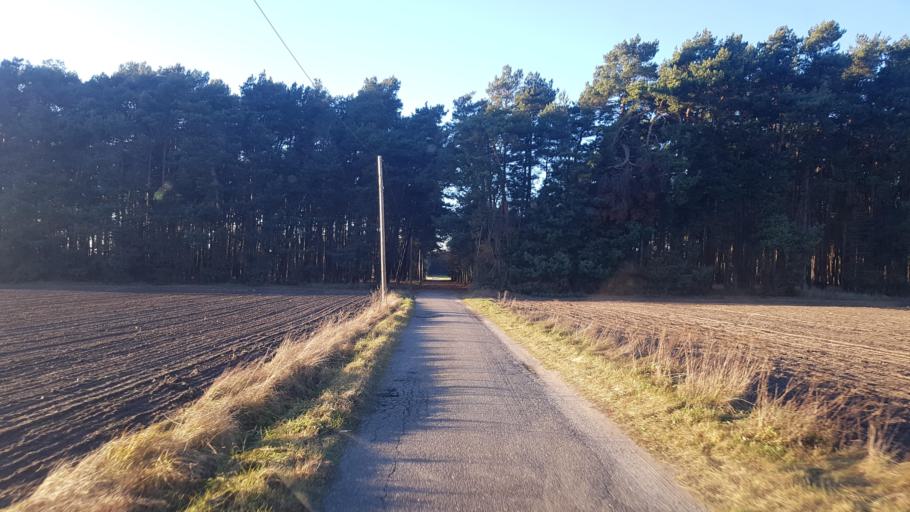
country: DE
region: Brandenburg
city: Peitz
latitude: 51.8867
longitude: 14.3976
